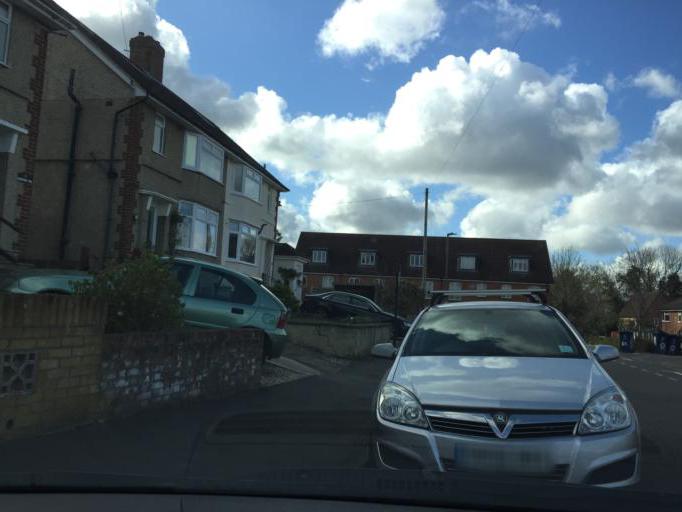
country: GB
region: England
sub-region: Oxfordshire
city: Oxford
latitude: 51.7648
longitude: -1.2326
